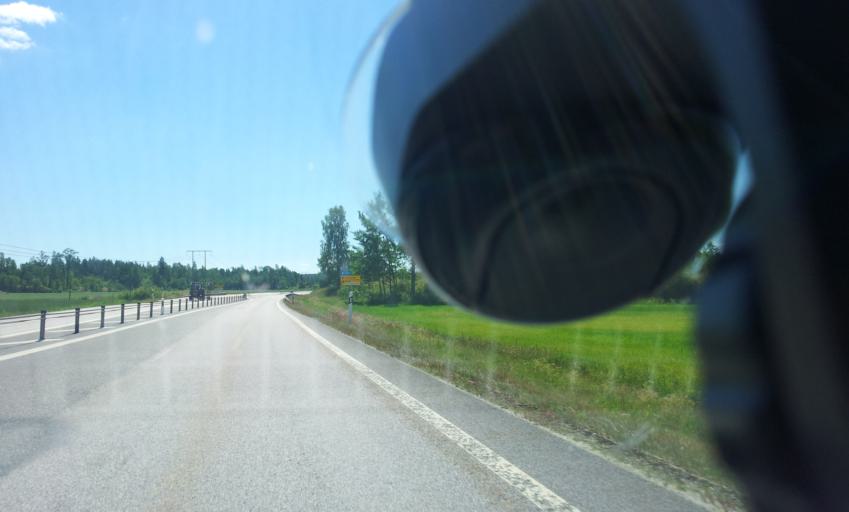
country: SE
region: OEstergoetland
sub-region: Valdemarsviks Kommun
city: Valdemarsvik
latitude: 58.0870
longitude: 16.5223
